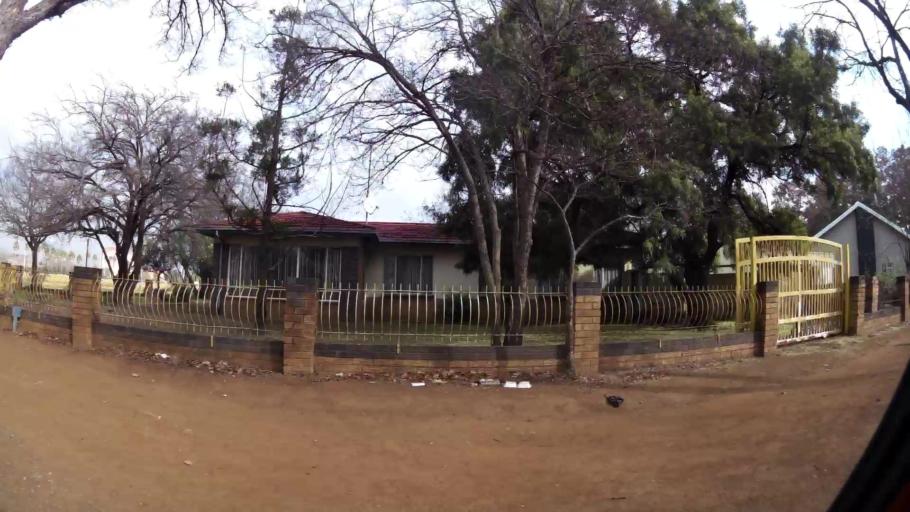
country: ZA
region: Gauteng
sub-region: Sedibeng District Municipality
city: Vanderbijlpark
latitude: -26.6928
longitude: 27.8388
